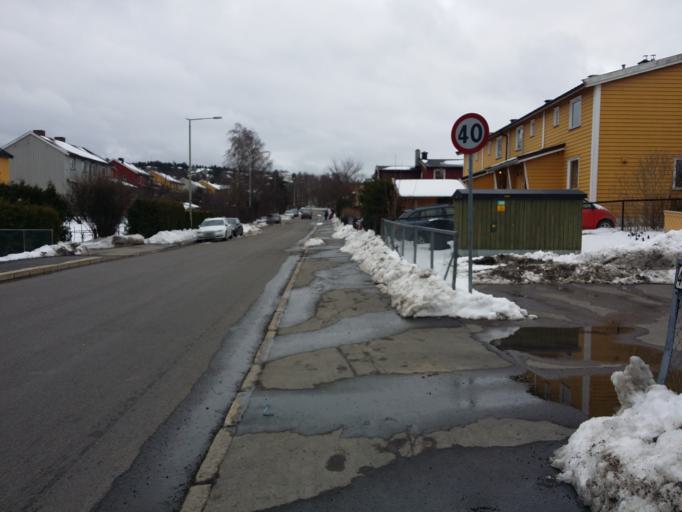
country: NO
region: Oslo
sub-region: Oslo
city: Oslo
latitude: 59.8972
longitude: 10.7817
